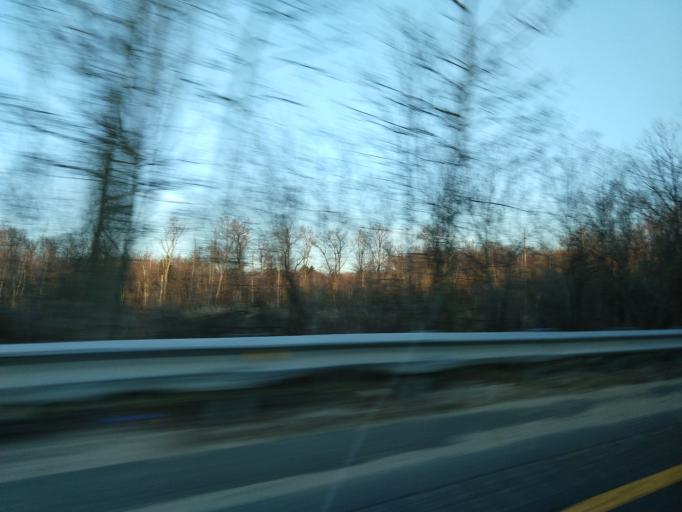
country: US
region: Massachusetts
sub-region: Essex County
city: South Peabody
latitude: 42.5289
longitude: -70.9765
